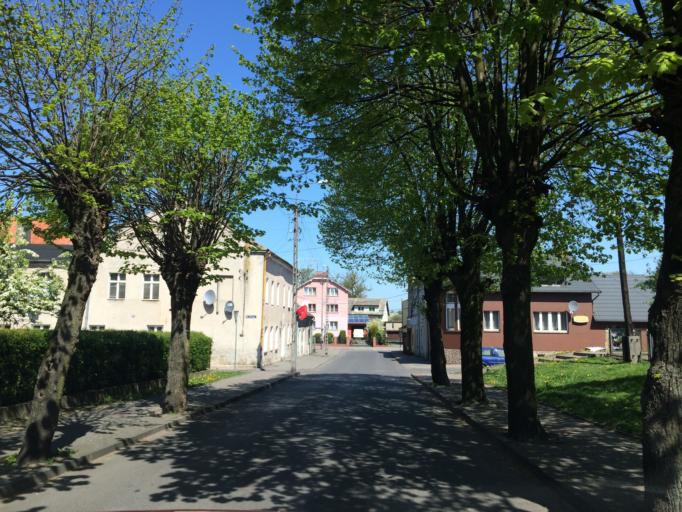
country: PL
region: Warmian-Masurian Voivodeship
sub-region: Powiat nowomiejski
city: Biskupiec
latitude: 53.5011
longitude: 19.3506
